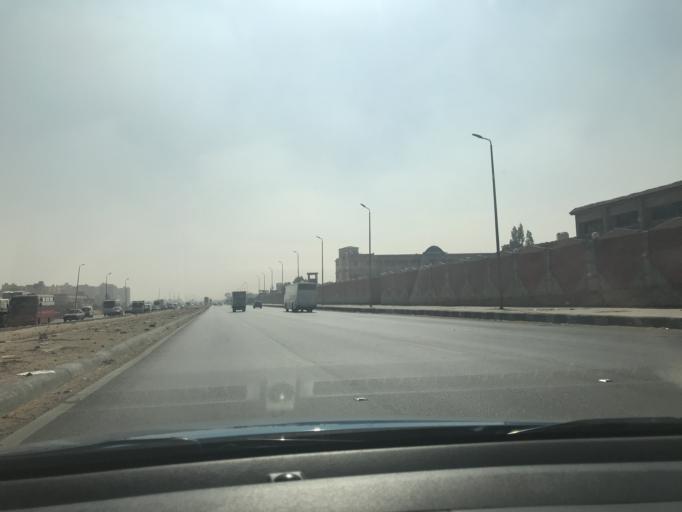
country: EG
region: Muhafazat al Qalyubiyah
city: Al Khankah
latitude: 30.1539
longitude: 31.4429
